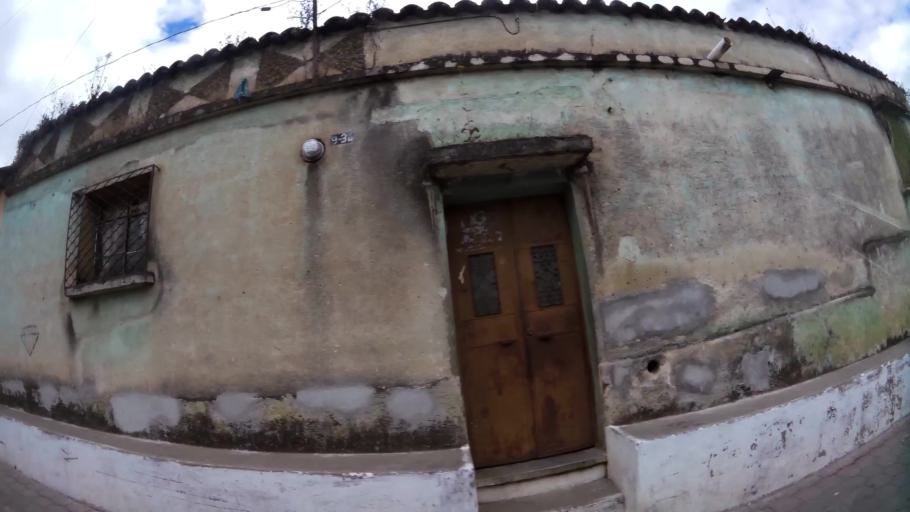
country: GT
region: Guatemala
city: Mixco
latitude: 14.6332
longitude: -90.6080
